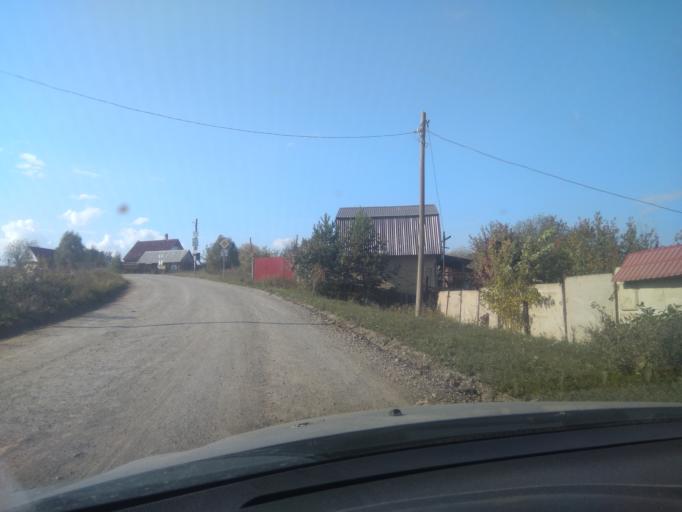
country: RU
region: Sverdlovsk
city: Pokrovskoye
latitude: 56.4365
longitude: 61.5904
